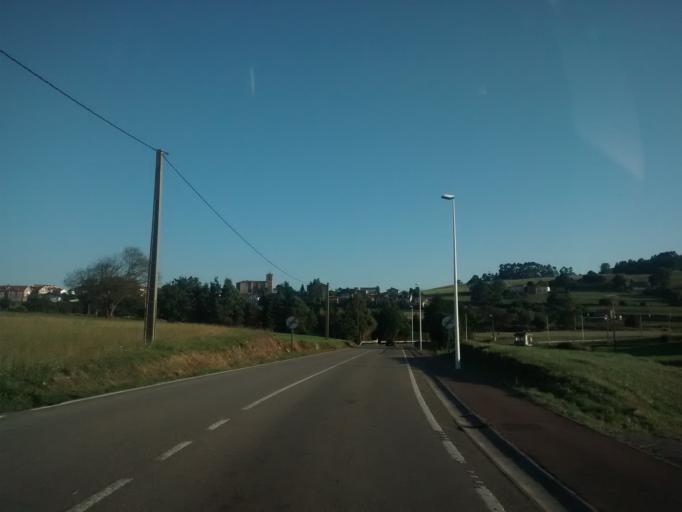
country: ES
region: Cantabria
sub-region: Provincia de Cantabria
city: San Miguel de Meruelo
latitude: 43.4512
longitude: -3.5721
